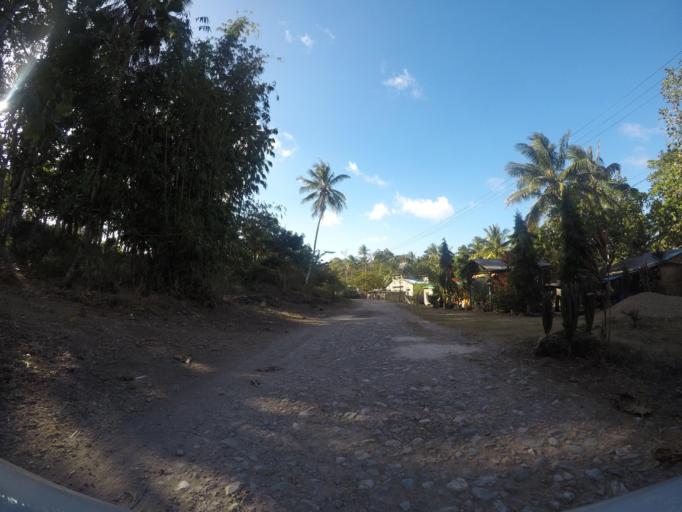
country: TL
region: Lautem
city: Lospalos
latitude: -8.4502
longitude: 126.8818
